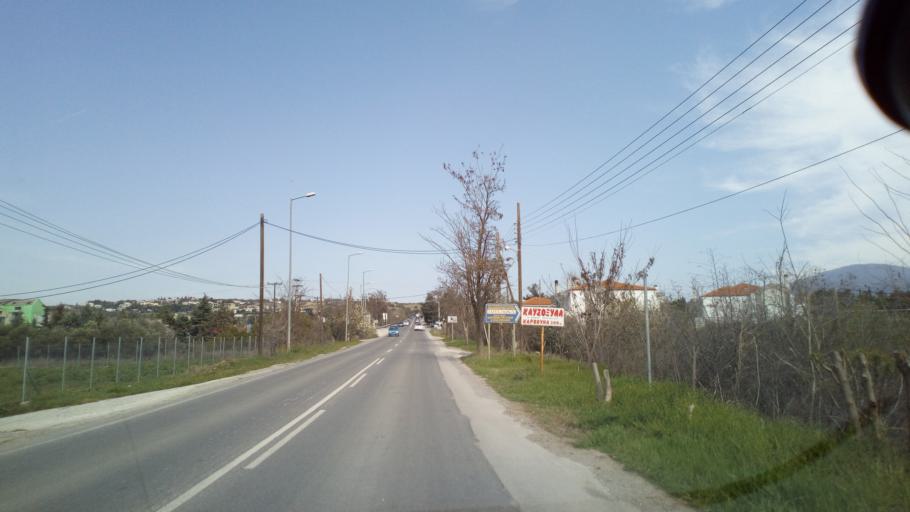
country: GR
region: Central Macedonia
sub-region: Nomos Thessalonikis
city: Thermi
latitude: 40.5590
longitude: 23.0215
